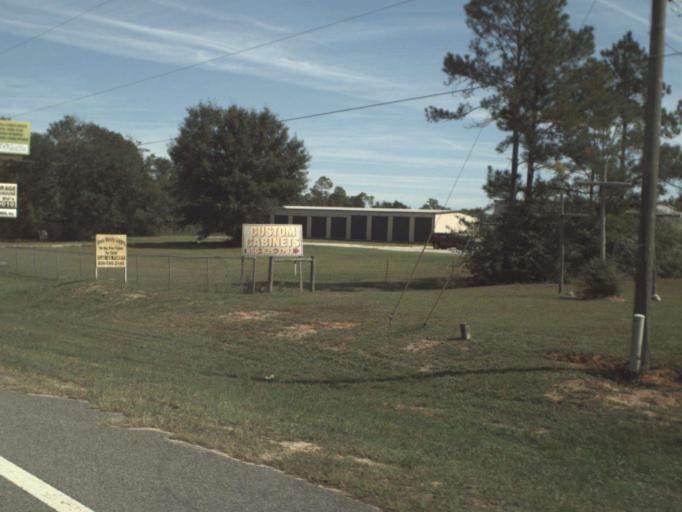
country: US
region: Florida
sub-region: Washington County
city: Chipley
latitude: 30.5832
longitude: -85.5931
